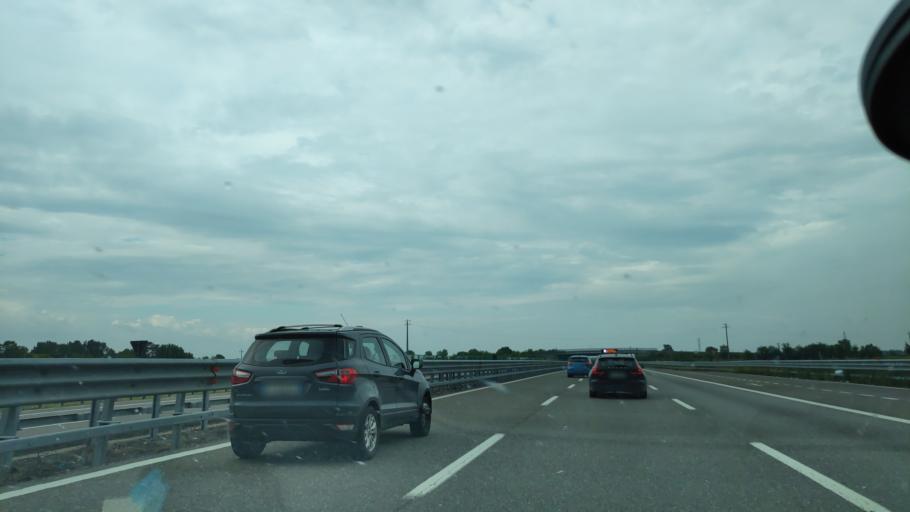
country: IT
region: Piedmont
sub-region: Provincia di Alessandria
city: Castelnuovo Scrivia
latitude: 44.9647
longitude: 8.8845
